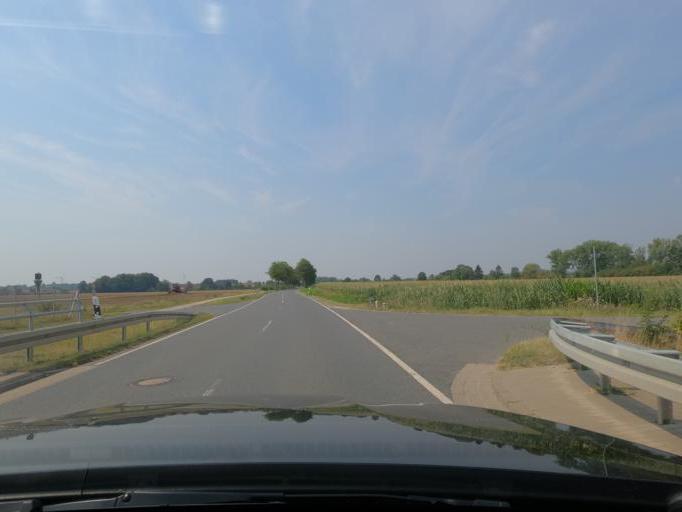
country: DE
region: Lower Saxony
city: Sehnde
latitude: 52.3017
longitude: 9.9565
